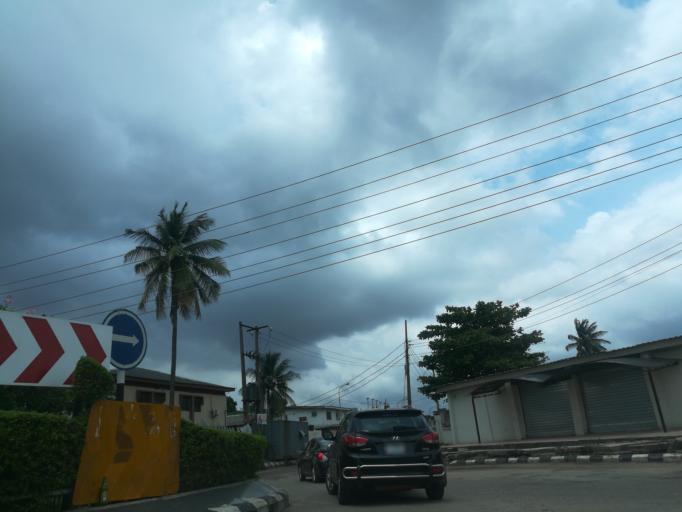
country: NG
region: Lagos
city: Somolu
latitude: 6.5520
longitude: 3.3621
